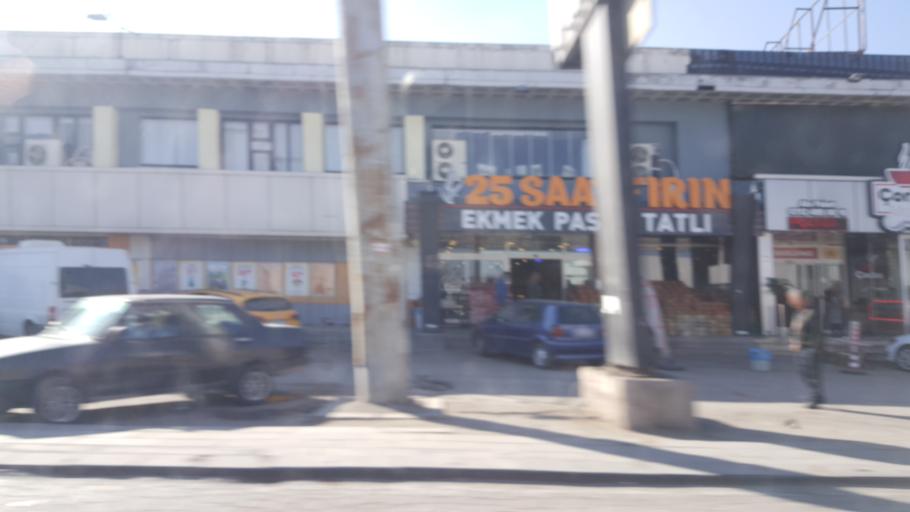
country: TR
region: Ankara
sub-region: Goelbasi
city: Golbasi
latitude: 39.8016
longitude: 32.8052
